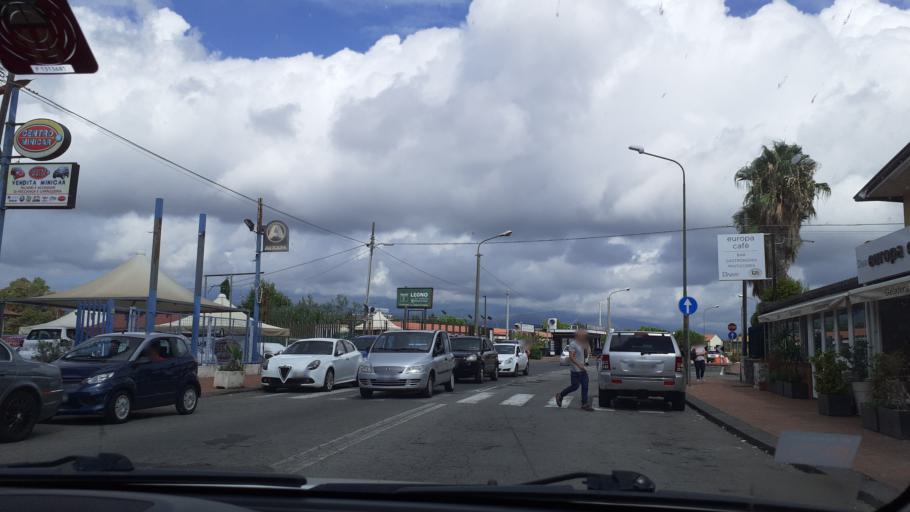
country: IT
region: Sicily
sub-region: Catania
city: San Gregorio di Catania
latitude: 37.5655
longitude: 15.1058
